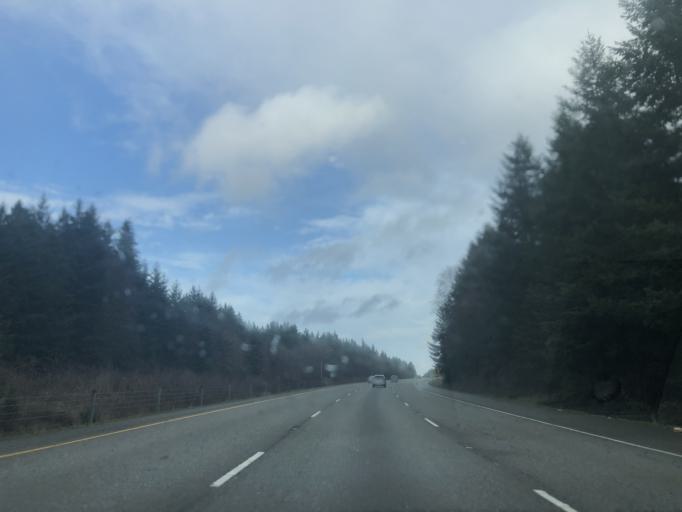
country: US
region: Washington
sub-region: Kitsap County
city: Silverdale
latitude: 47.6784
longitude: -122.6909
